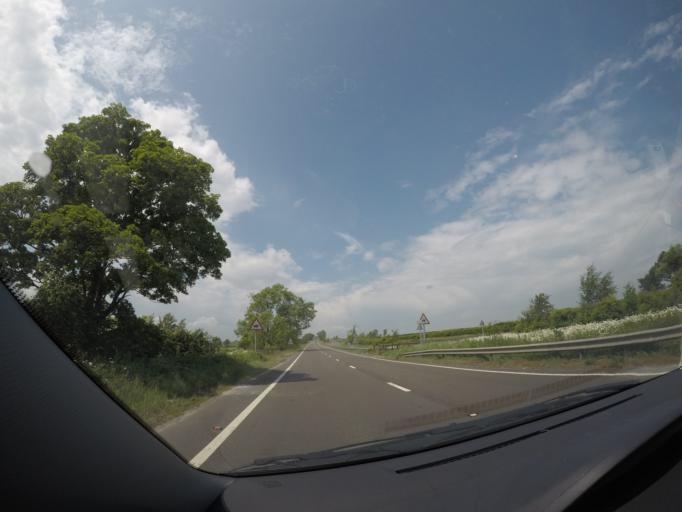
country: GB
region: England
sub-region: North Yorkshire
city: Catterick Garrison
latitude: 54.4541
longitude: -1.7062
